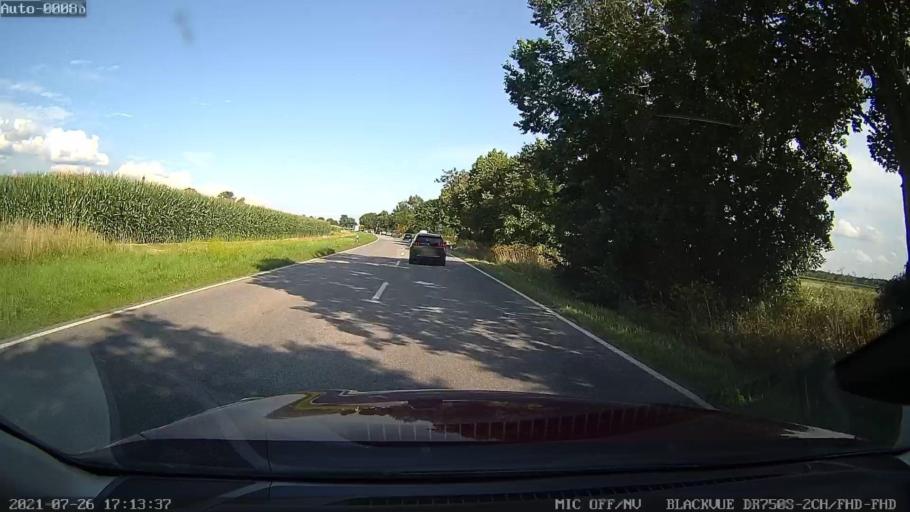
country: DE
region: Bavaria
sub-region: Upper Palatinate
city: Riekofen
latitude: 48.9690
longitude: 12.3200
